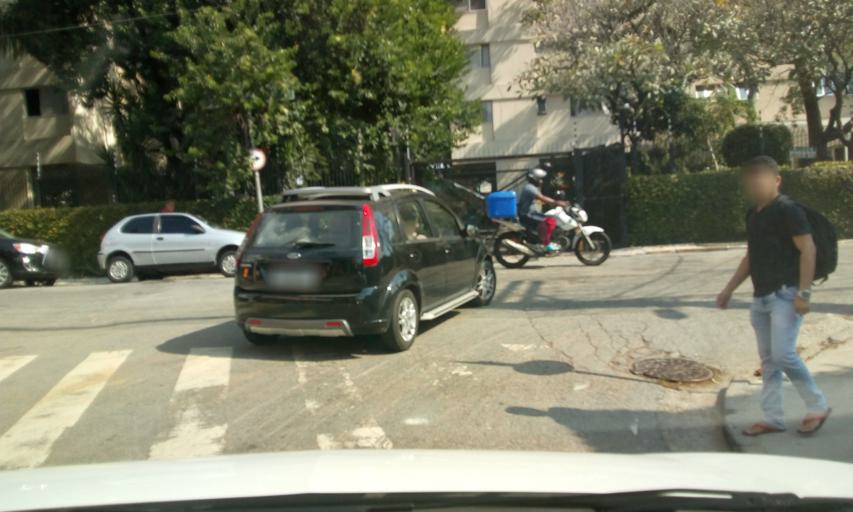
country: BR
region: Sao Paulo
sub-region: Sao Paulo
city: Sao Paulo
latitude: -23.6012
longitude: -46.6817
